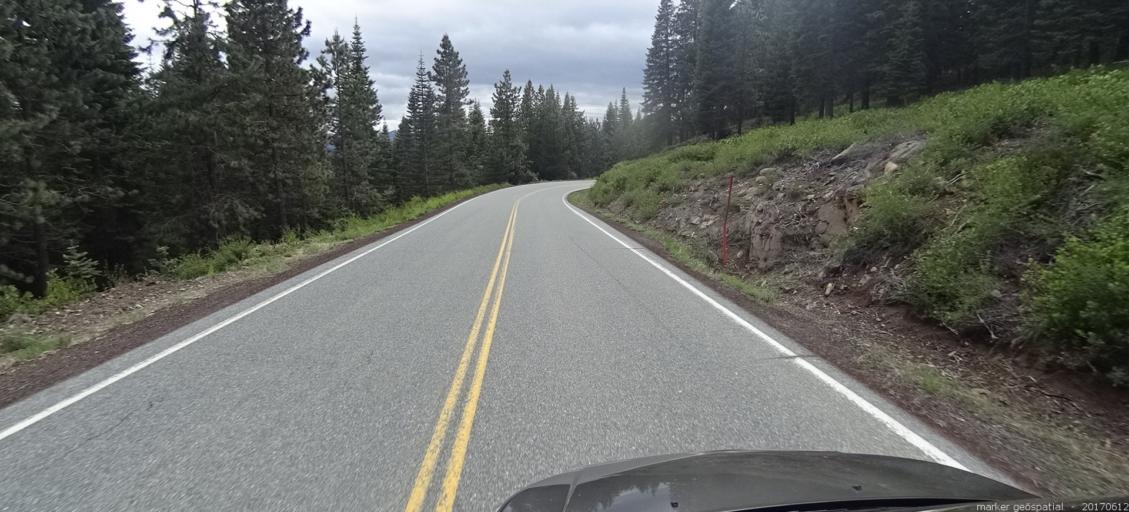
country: US
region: California
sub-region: Siskiyou County
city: Mount Shasta
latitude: 41.3301
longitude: -122.2511
